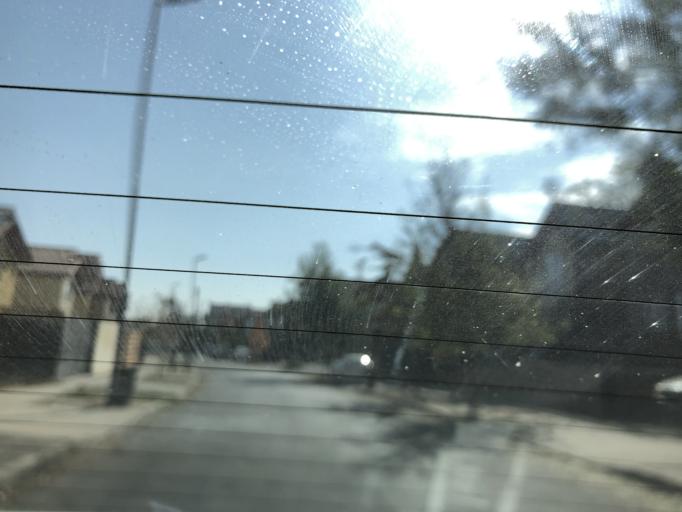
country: CL
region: Santiago Metropolitan
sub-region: Provincia de Cordillera
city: Puente Alto
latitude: -33.5723
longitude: -70.5365
